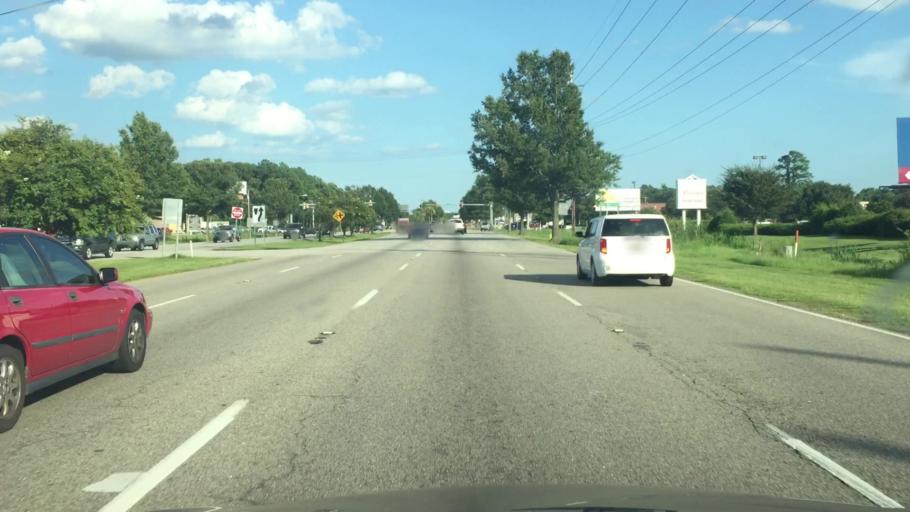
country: US
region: South Carolina
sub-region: Horry County
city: Myrtle Beach
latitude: 33.7076
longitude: -78.9124
